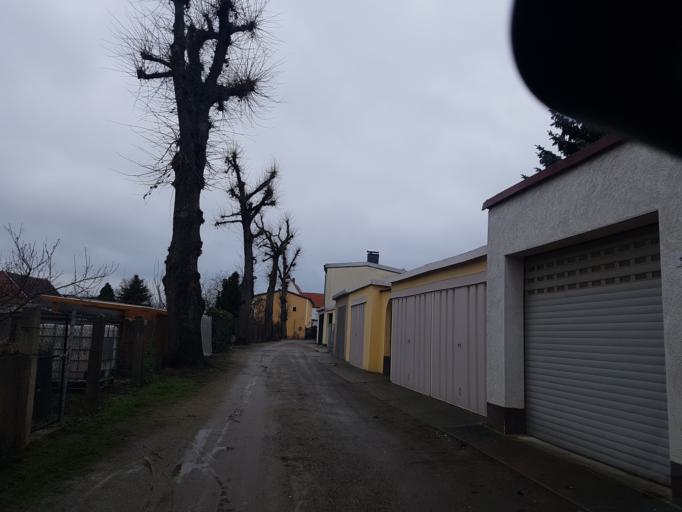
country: DE
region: Brandenburg
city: Muhlberg
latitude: 51.4328
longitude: 13.2185
